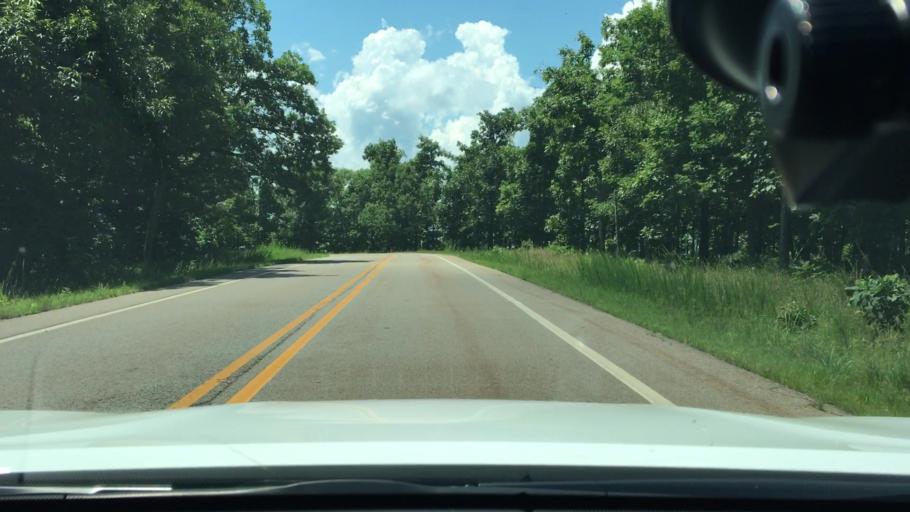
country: US
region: Arkansas
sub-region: Logan County
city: Paris
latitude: 35.1657
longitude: -93.6522
